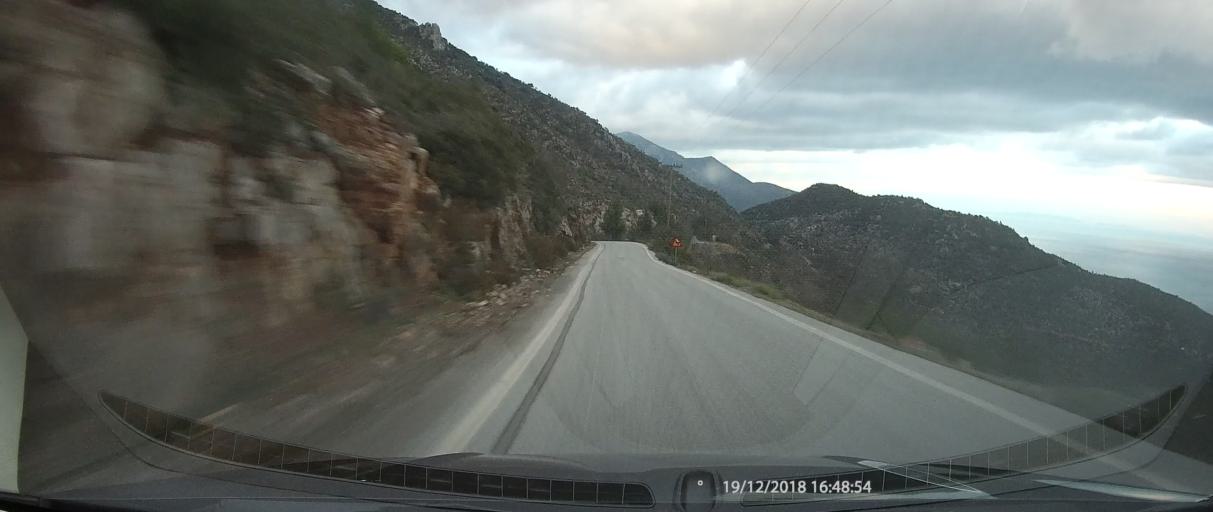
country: GR
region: Peloponnese
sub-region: Nomos Lakonias
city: Sykea
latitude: 36.9411
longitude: 22.9965
